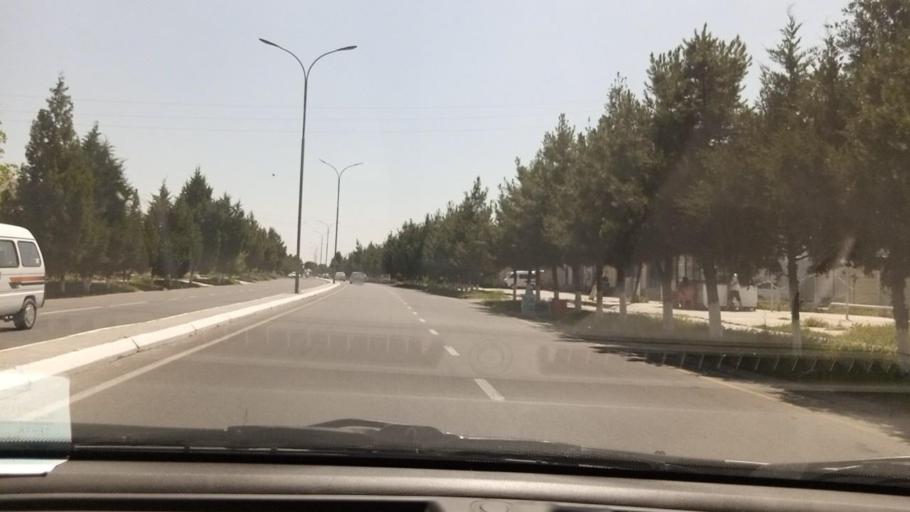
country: UZ
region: Toshkent
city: Urtaowul
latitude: 41.2145
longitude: 69.1726
